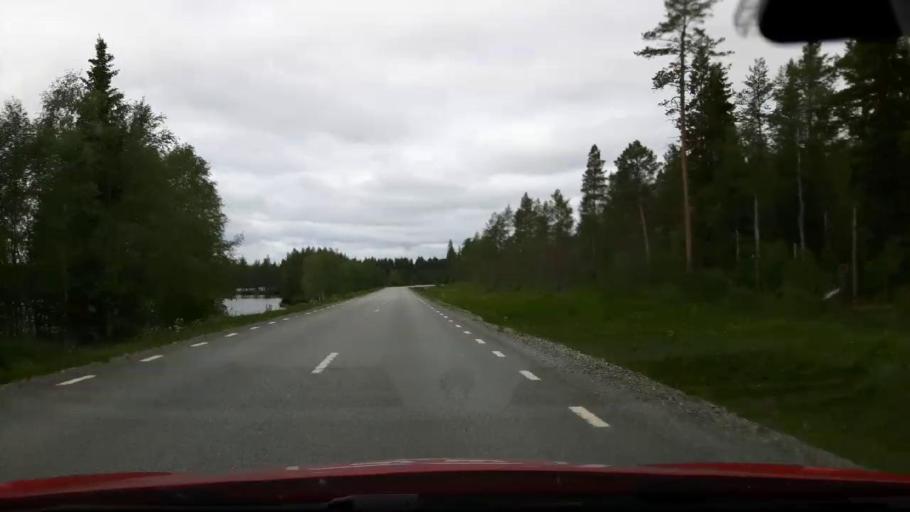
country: SE
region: Jaemtland
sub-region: OEstersunds Kommun
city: Lit
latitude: 63.6813
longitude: 14.6778
